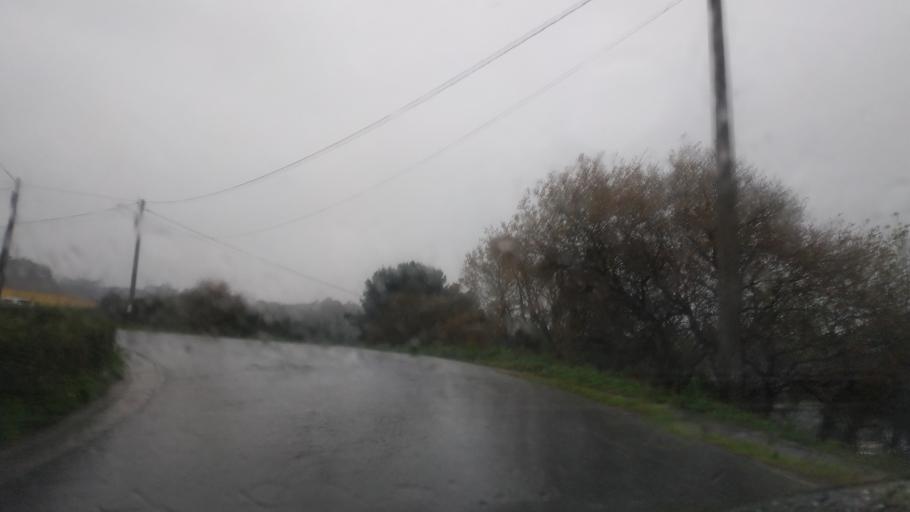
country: ES
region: Galicia
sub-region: Provincia da Coruna
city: A Coruna
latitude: 43.3319
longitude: -8.4089
